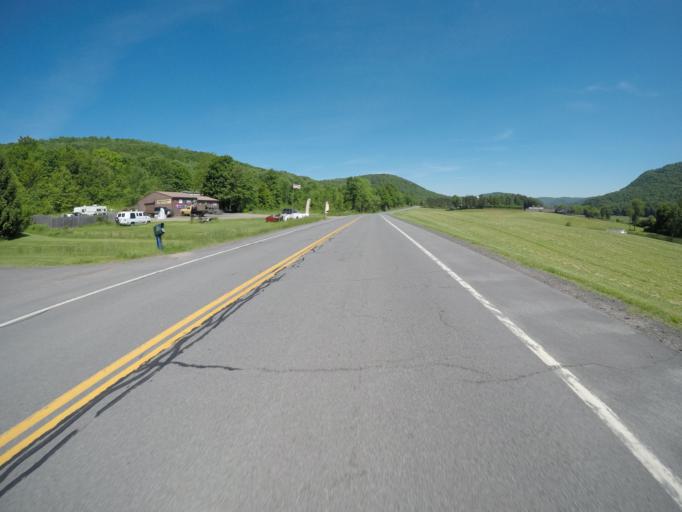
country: US
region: New York
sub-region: Delaware County
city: Delhi
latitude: 42.2215
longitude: -74.9681
